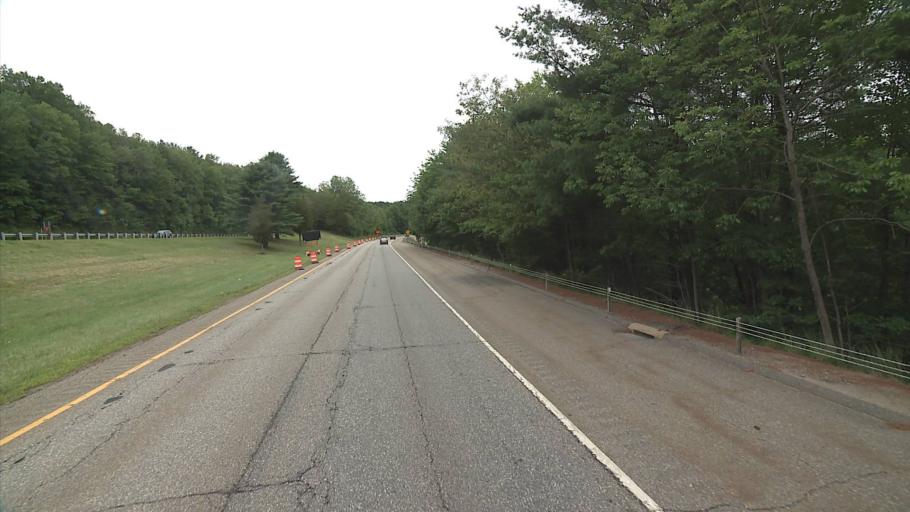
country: US
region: Connecticut
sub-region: Litchfield County
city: Northwest Harwinton
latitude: 41.7272
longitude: -73.1024
